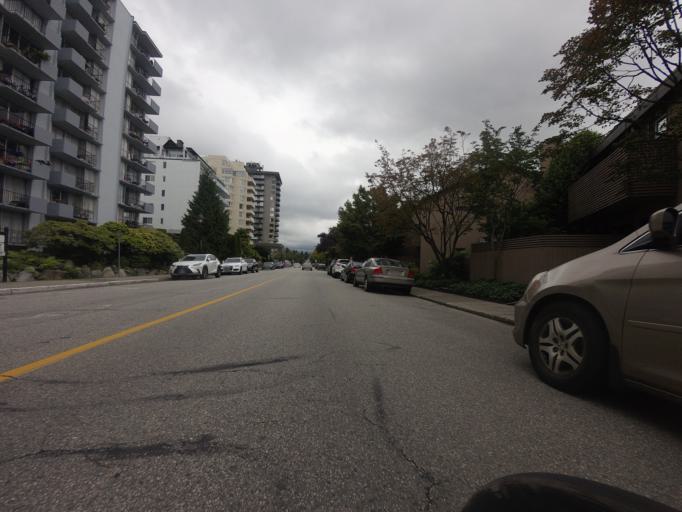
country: CA
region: British Columbia
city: West Vancouver
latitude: 49.3277
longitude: -123.1638
